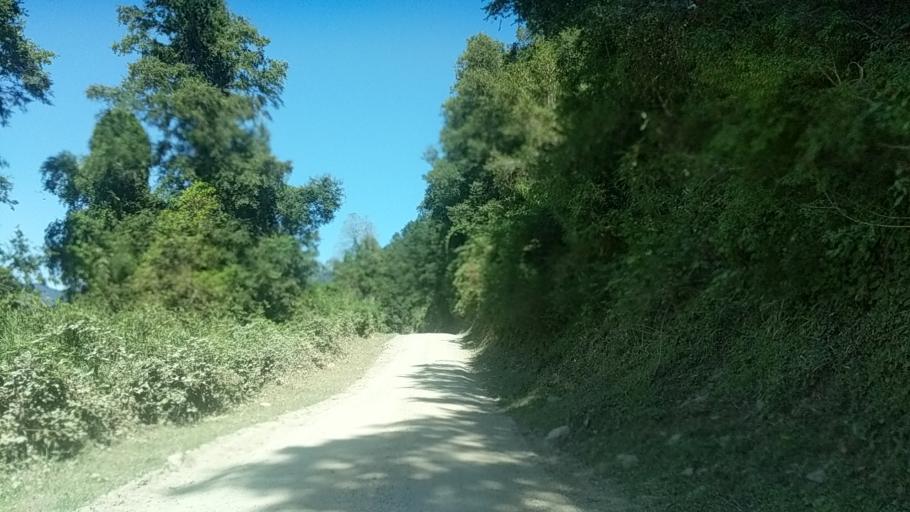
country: CL
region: Araucania
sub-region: Provincia de Cautin
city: Pucon
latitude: -39.0622
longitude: -71.7074
